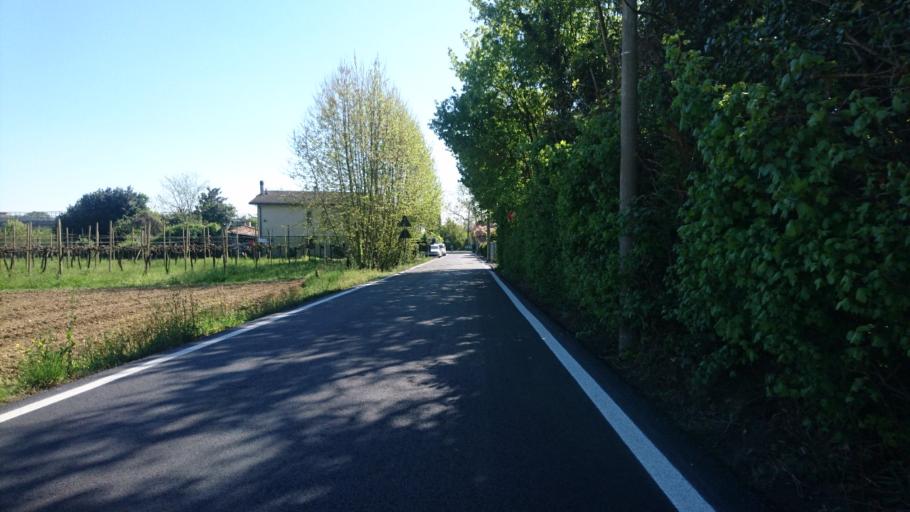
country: IT
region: Veneto
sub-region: Provincia di Treviso
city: Mogliano Veneto
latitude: 45.5142
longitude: 12.2569
